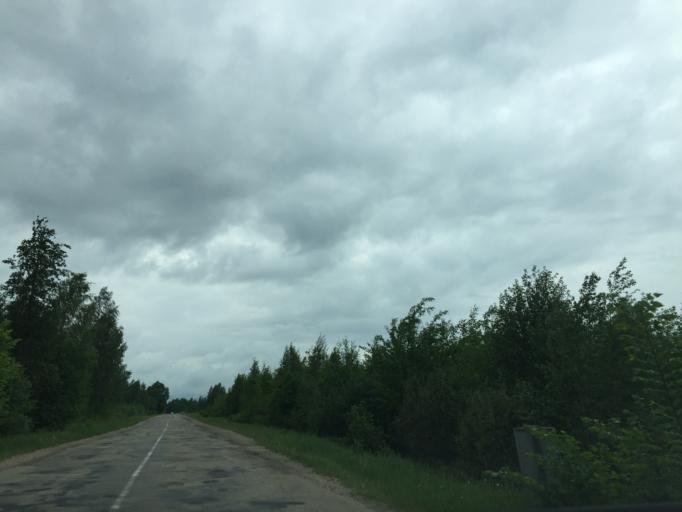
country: LV
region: Varkava
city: Vecvarkava
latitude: 56.0917
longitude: 26.5674
